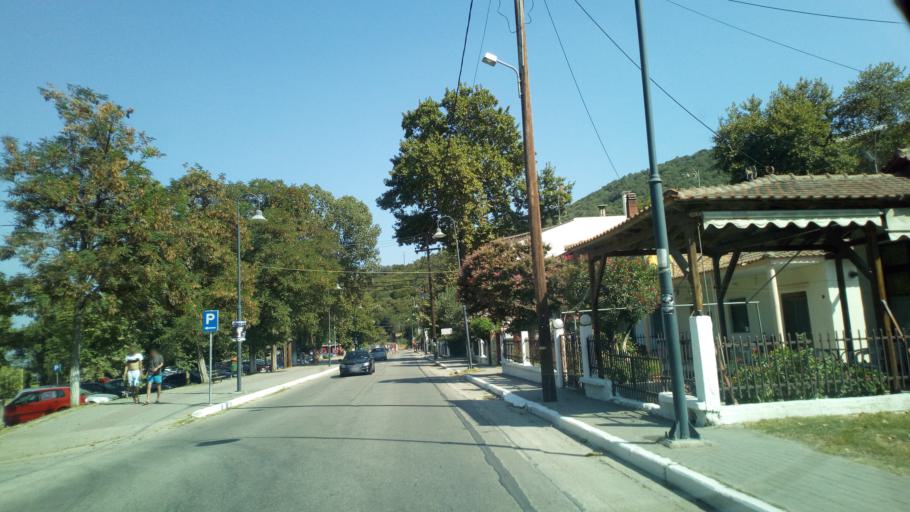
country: GR
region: Central Macedonia
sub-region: Nomos Thessalonikis
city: Stavros
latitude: 40.6631
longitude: 23.7068
